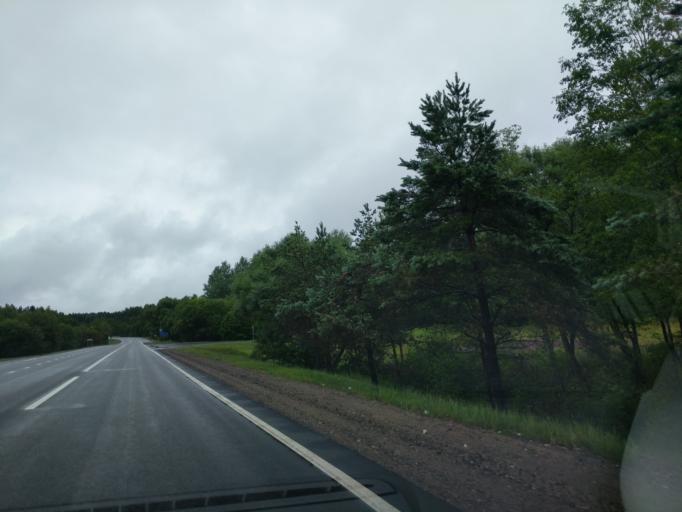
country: BY
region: Minsk
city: Syomkava
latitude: 54.2076
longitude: 27.4956
